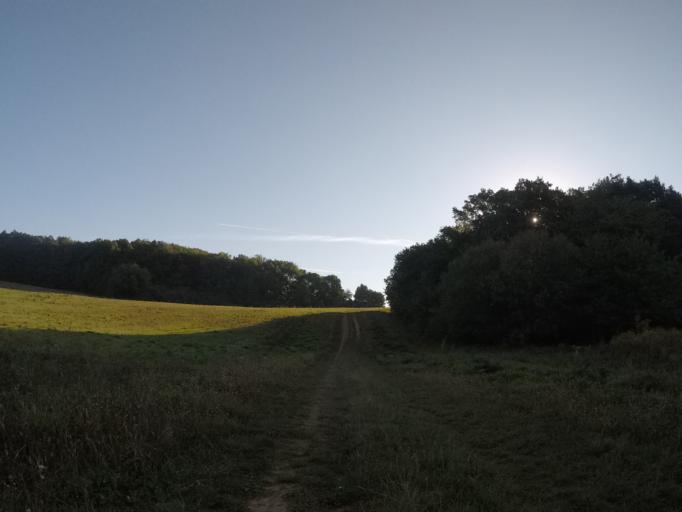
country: SK
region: Kosicky
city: Kosice
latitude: 48.7323
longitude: 21.1898
